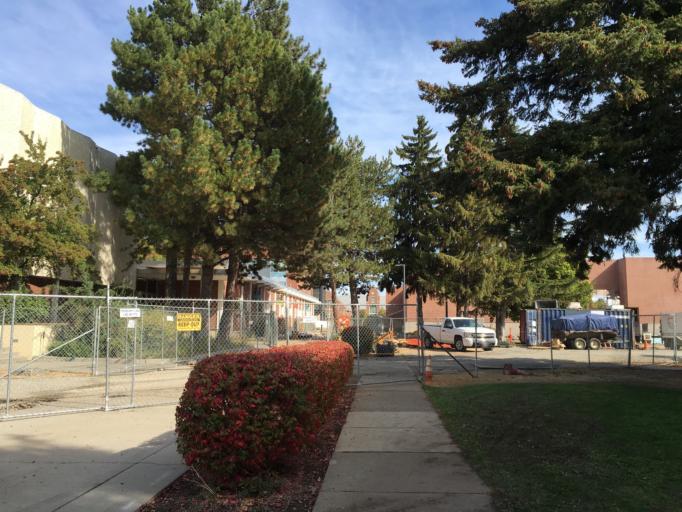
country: US
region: Washington
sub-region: Kittitas County
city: Ellensburg
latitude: 47.0017
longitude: -120.5421
